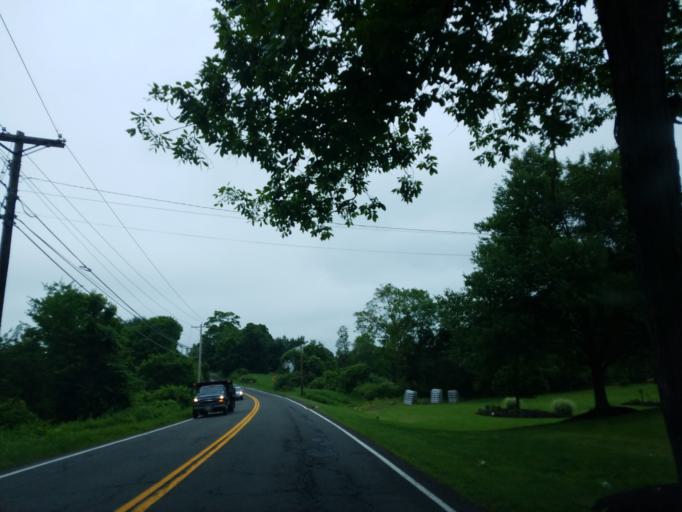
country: US
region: Connecticut
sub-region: New Haven County
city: Heritage Village
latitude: 41.4784
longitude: -73.2548
